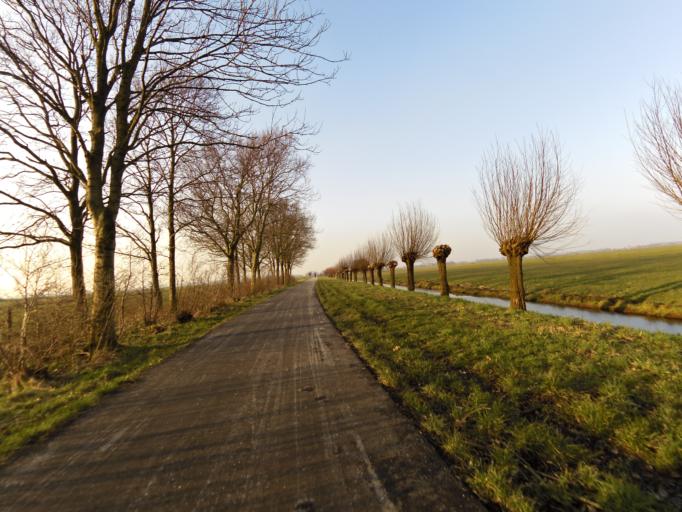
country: NL
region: South Holland
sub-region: Gemeente Leiderdorp
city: Leiderdorp
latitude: 52.1398
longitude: 4.5896
